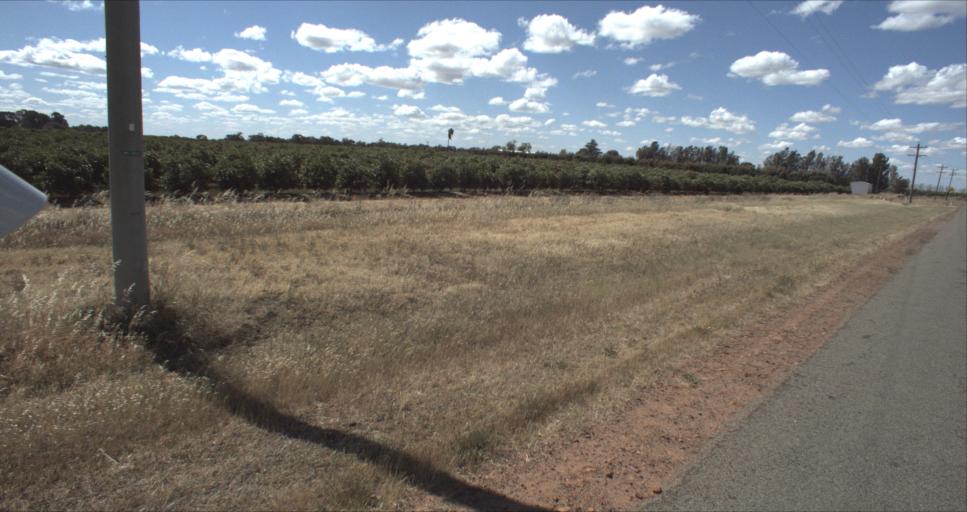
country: AU
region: New South Wales
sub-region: Leeton
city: Leeton
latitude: -34.5141
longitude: 146.2399
